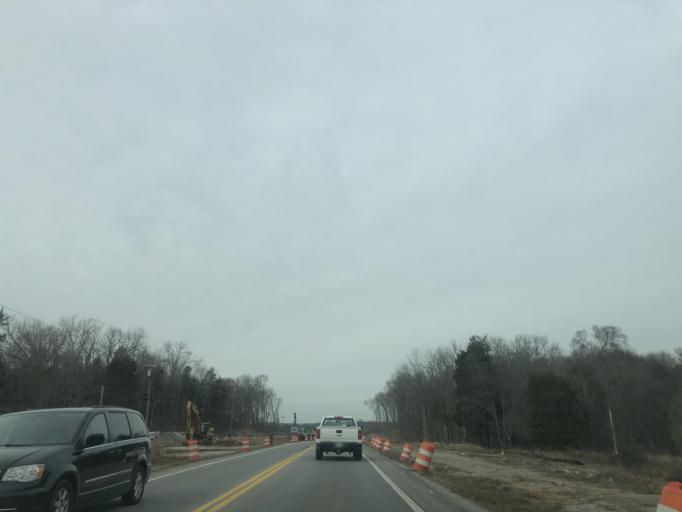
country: US
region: Tennessee
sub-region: Wilson County
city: Mount Juliet
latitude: 36.2732
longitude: -86.4418
